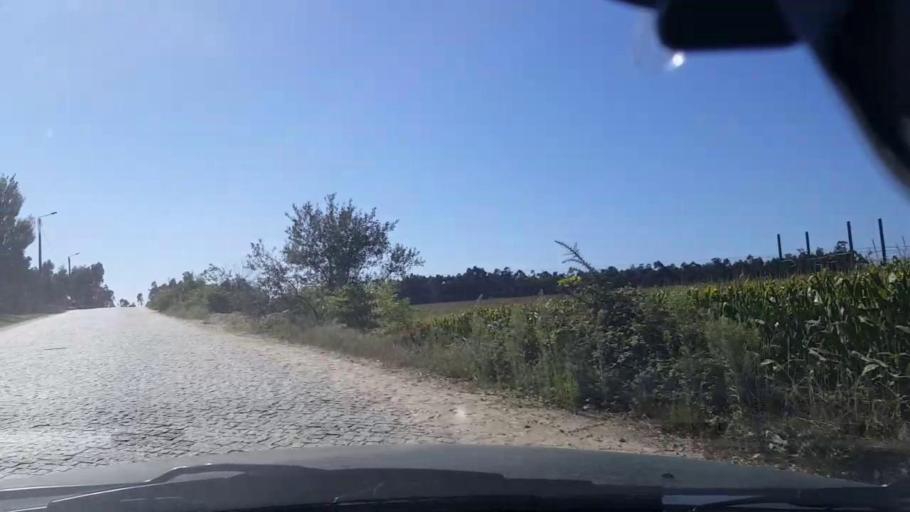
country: PT
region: Porto
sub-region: Matosinhos
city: Lavra
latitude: 41.2866
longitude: -8.6935
